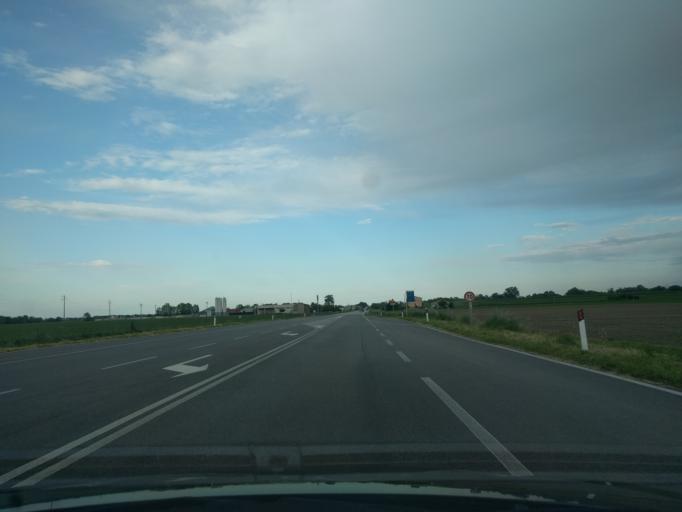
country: IT
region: Veneto
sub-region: Provincia di Rovigo
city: Canaro
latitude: 44.9256
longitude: 11.6895
